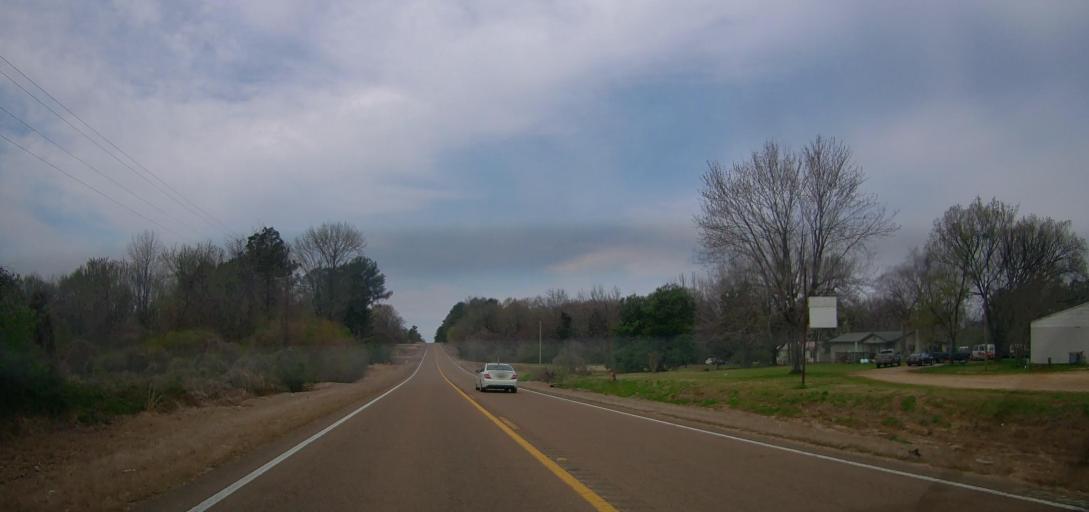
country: US
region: Mississippi
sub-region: Marshall County
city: Byhalia
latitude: 34.8372
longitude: -89.5914
